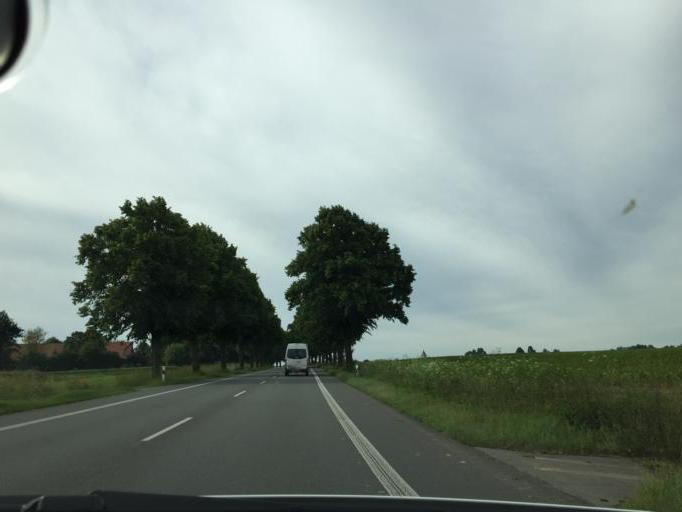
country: DE
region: North Rhine-Westphalia
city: Warburg
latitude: 51.5416
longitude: 9.1336
